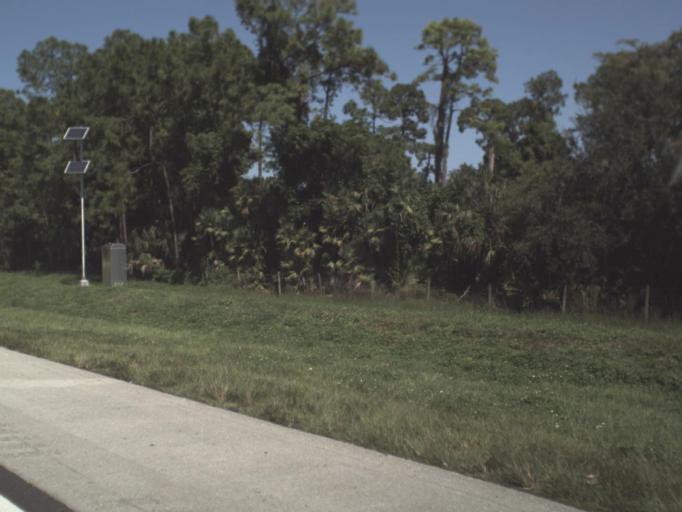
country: US
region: Florida
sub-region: Lee County
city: Bonita Springs
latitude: 26.2874
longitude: -81.7426
